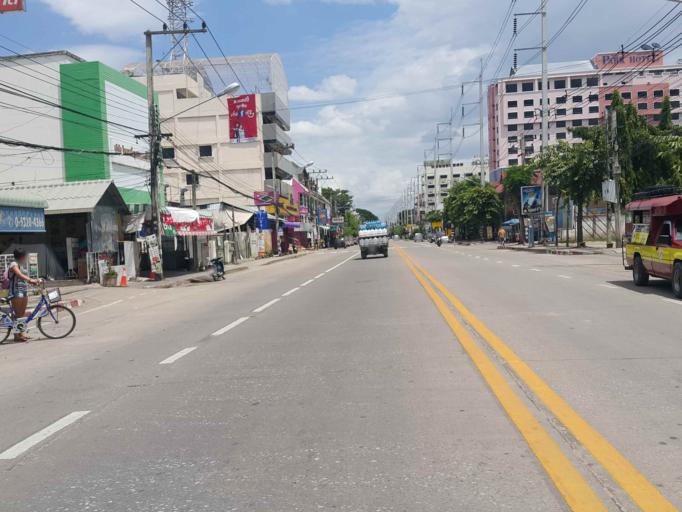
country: TH
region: Chiang Mai
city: Chiang Mai
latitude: 18.7684
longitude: 98.9991
